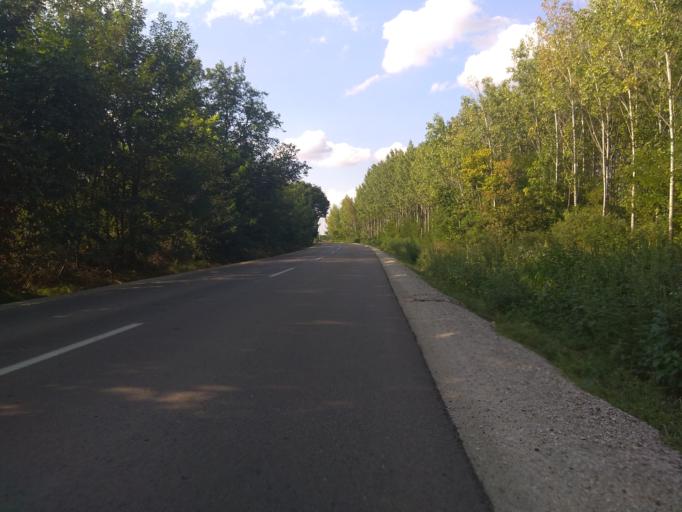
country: HU
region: Borsod-Abauj-Zemplen
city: Hejobaba
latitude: 47.8883
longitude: 20.8968
